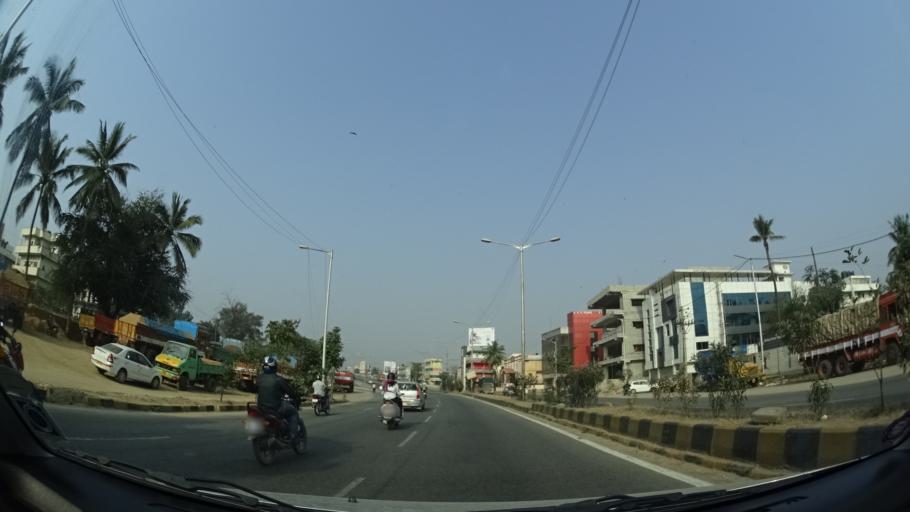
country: IN
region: Karnataka
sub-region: Bangalore Urban
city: Yelahanka
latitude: 13.0471
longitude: 77.5800
